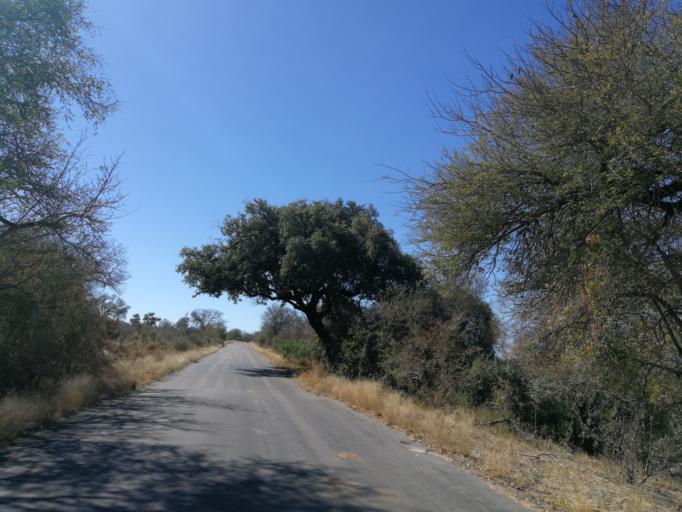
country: ZA
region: Limpopo
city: Thulamahashi
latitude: -24.9548
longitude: 31.6498
